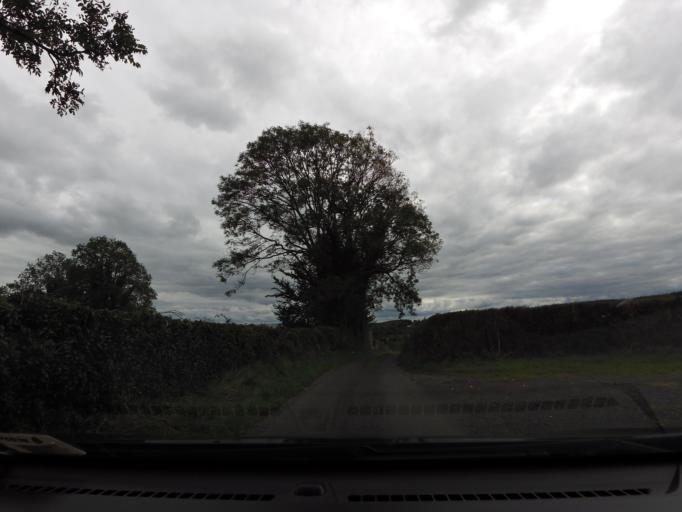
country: IE
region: Connaught
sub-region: County Galway
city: Loughrea
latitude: 53.1576
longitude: -8.4700
